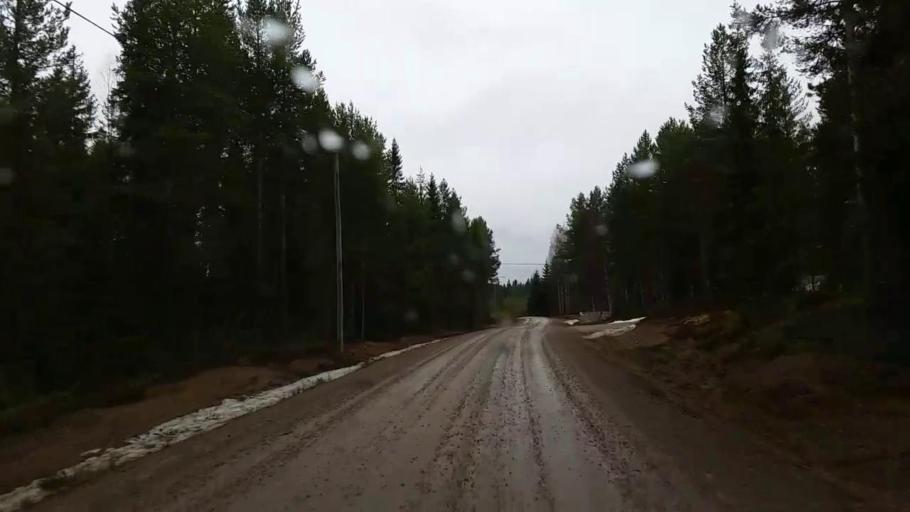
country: SE
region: Gaevleborg
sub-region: Ljusdals Kommun
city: Farila
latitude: 62.1353
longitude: 15.6613
